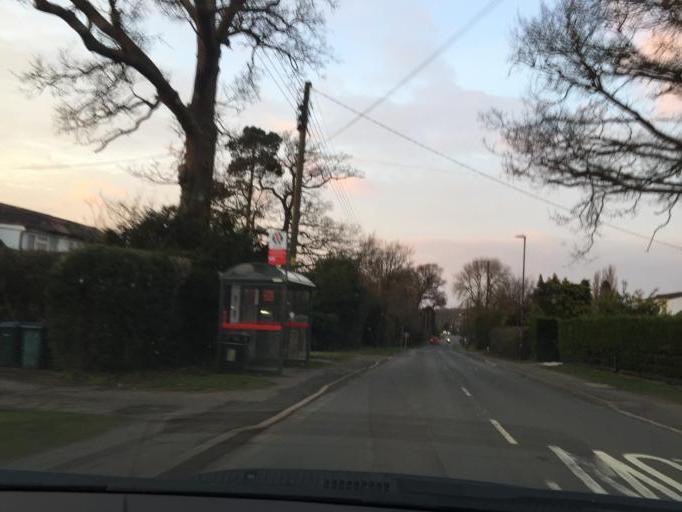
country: GB
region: England
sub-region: Warwickshire
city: Kenilworth
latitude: 52.3897
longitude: -1.5986
